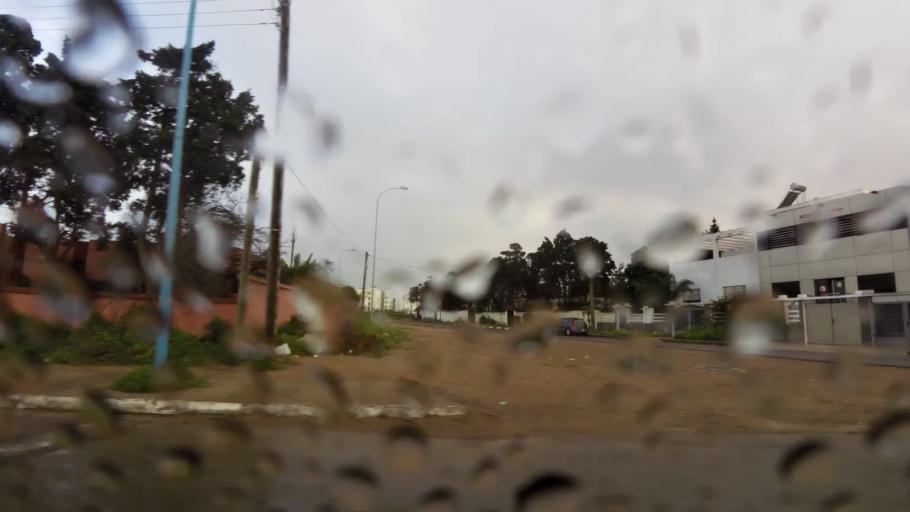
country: MA
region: Doukkala-Abda
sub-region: El-Jadida
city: El Jadida
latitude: 33.2374
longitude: -8.5196
